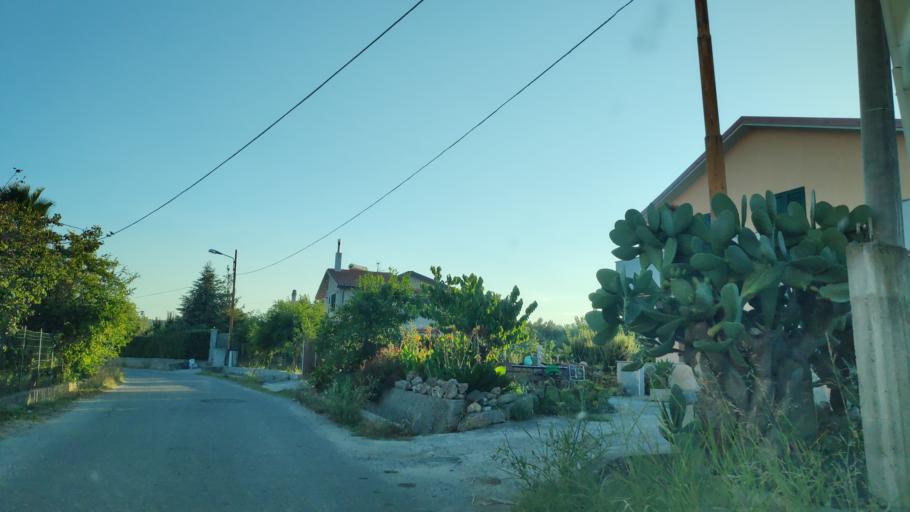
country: IT
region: Calabria
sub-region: Provincia di Reggio Calabria
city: Monasterace Marina
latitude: 38.4315
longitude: 16.5632
